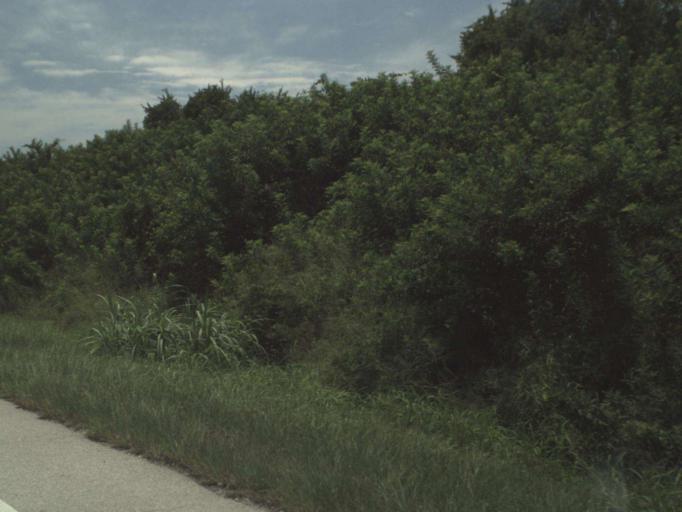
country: US
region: Florida
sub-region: Okeechobee County
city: Taylor Creek
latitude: 27.1014
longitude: -80.6583
